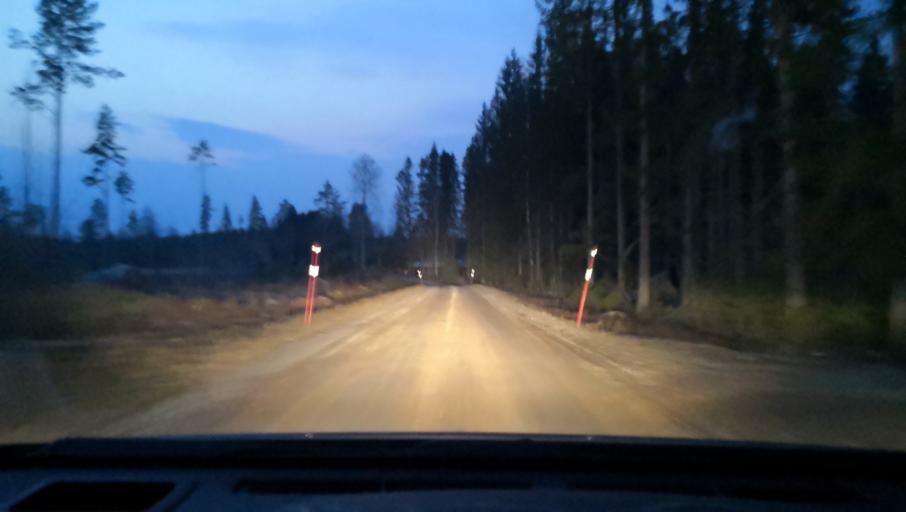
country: SE
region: OErebro
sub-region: Lindesbergs Kommun
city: Frovi
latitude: 59.5917
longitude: 15.4699
